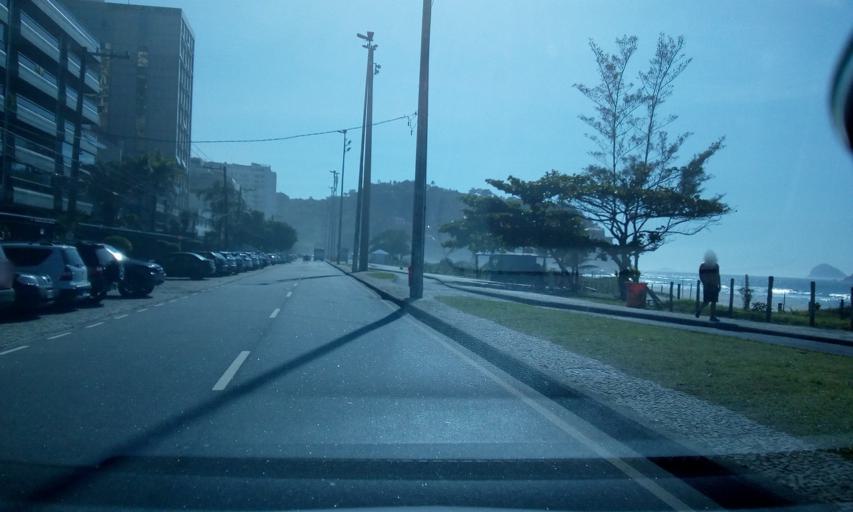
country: BR
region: Rio de Janeiro
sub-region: Rio De Janeiro
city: Rio de Janeiro
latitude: -23.0149
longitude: -43.3032
